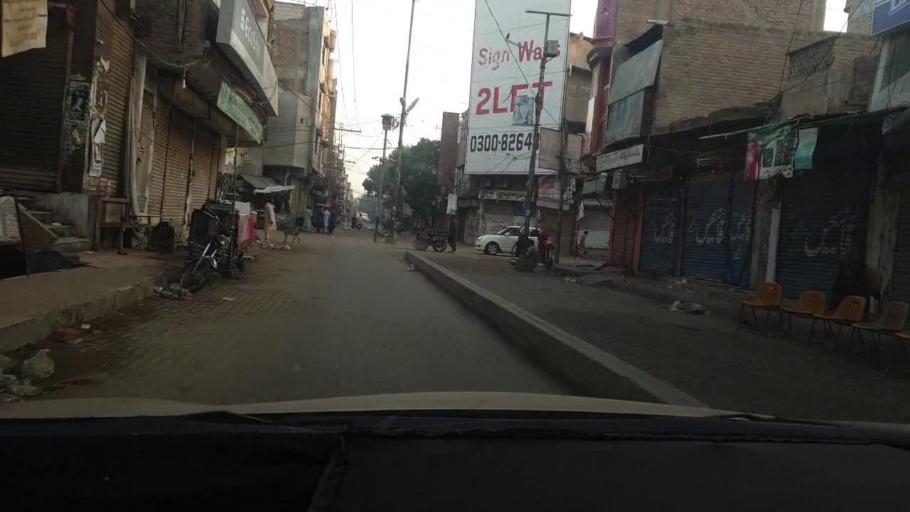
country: PK
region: Sindh
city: Larkana
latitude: 27.5525
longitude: 68.2152
